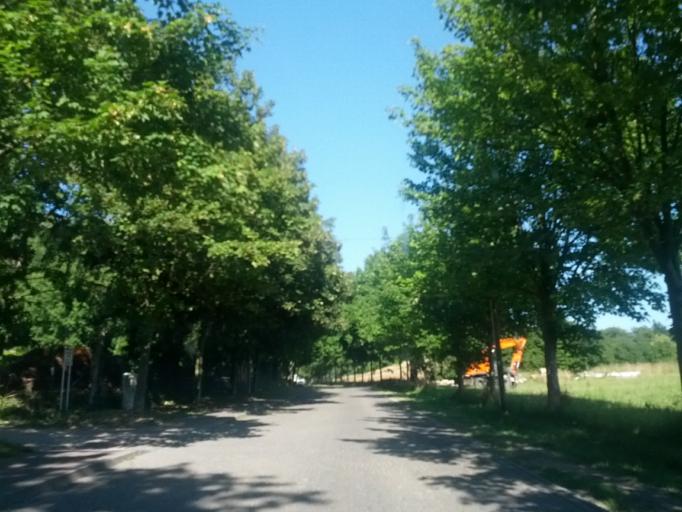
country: DE
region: Mecklenburg-Vorpommern
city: Ostseebad Gohren
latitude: 54.3393
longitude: 13.7291
